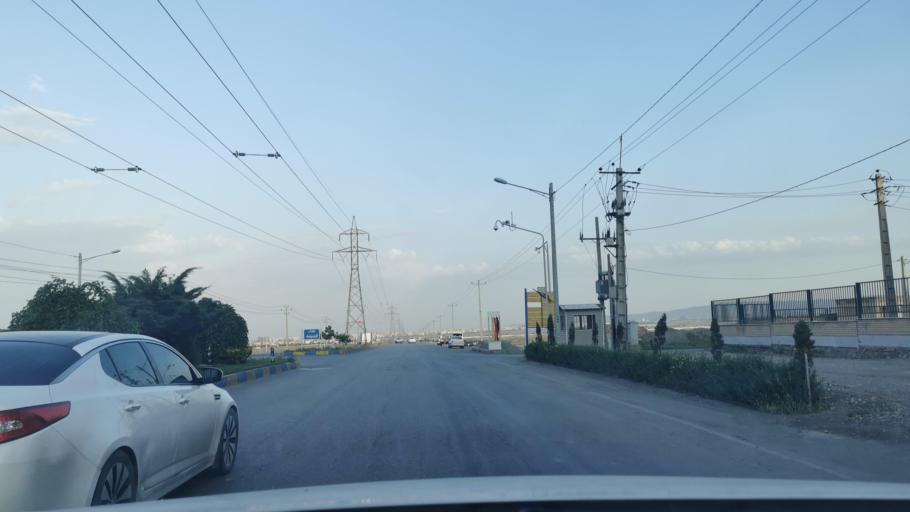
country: IR
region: Razavi Khorasan
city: Torqabeh
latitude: 36.4223
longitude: 59.4268
